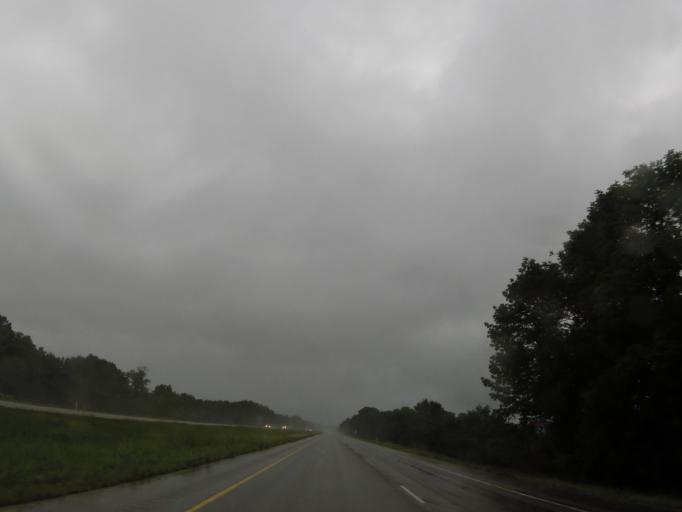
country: US
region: Illinois
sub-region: Johnson County
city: Vienna
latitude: 37.4538
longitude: -88.8882
